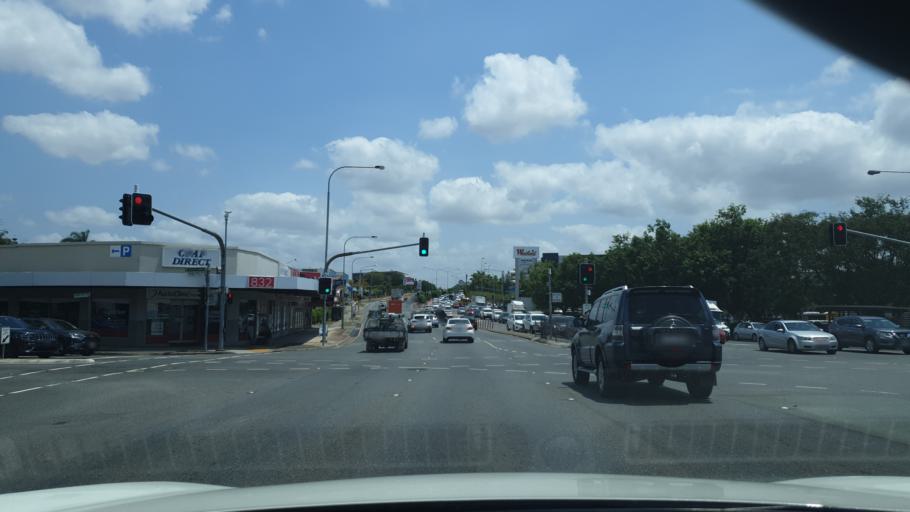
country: AU
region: Queensland
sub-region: Brisbane
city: Chermside West
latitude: -27.3861
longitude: 153.0308
